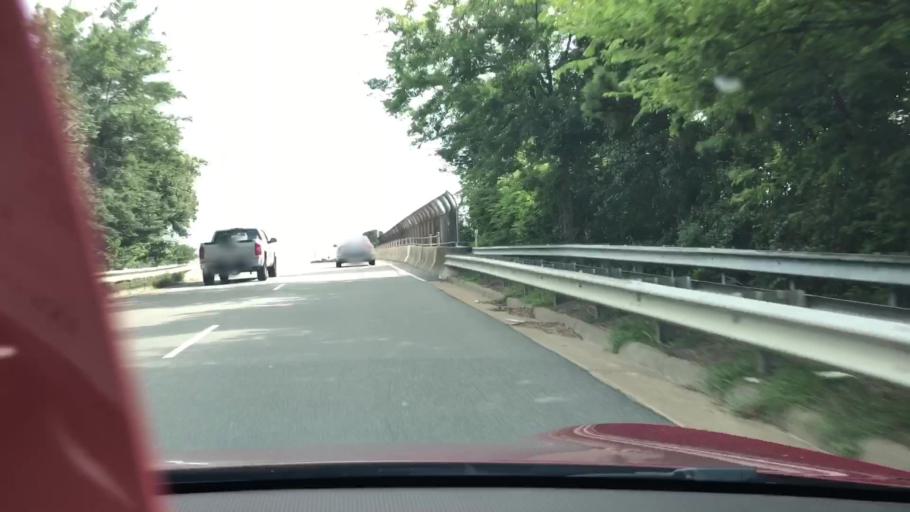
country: US
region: Virginia
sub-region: City of Virginia Beach
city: Virginia Beach
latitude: 36.9056
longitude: -76.0675
